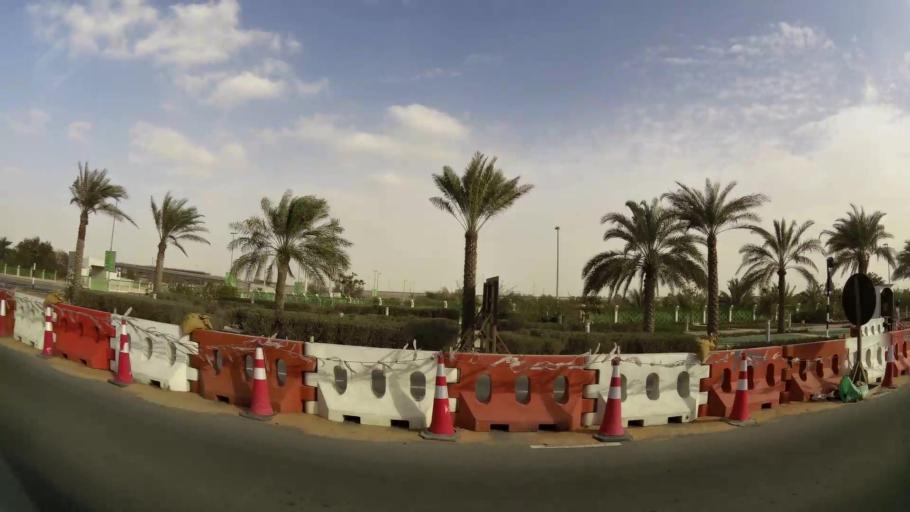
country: AE
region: Abu Dhabi
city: Abu Dhabi
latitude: 24.4554
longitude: 54.6185
